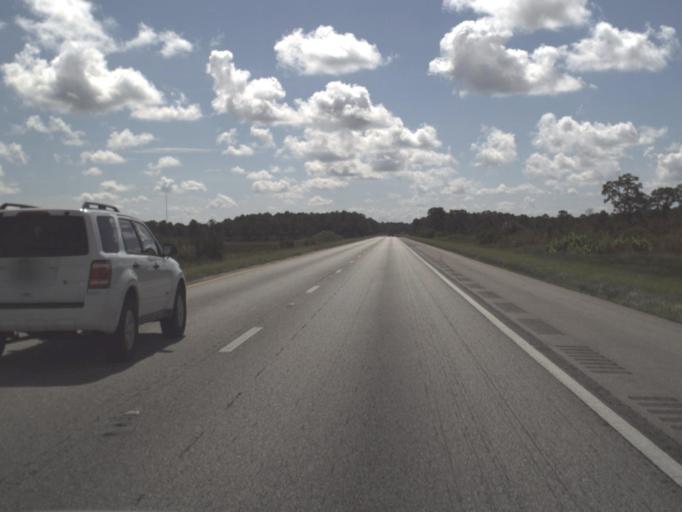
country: US
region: Florida
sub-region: Lee County
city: Suncoast Estates
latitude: 26.8028
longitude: -81.9218
